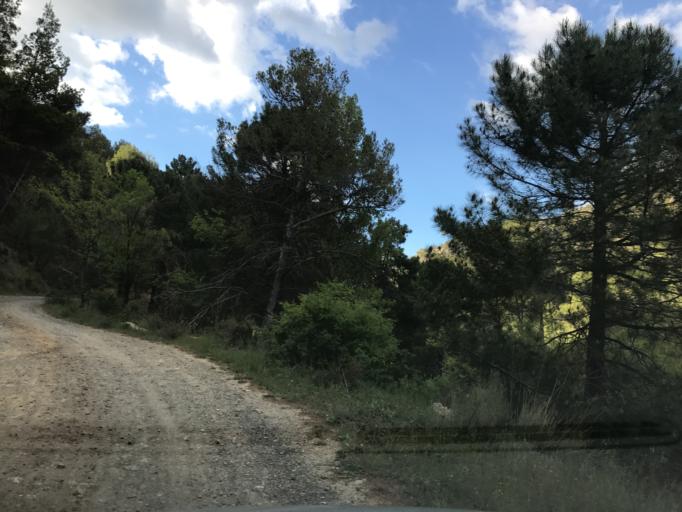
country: ES
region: Andalusia
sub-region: Provincia de Granada
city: Quentar
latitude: 37.2267
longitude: -3.4094
